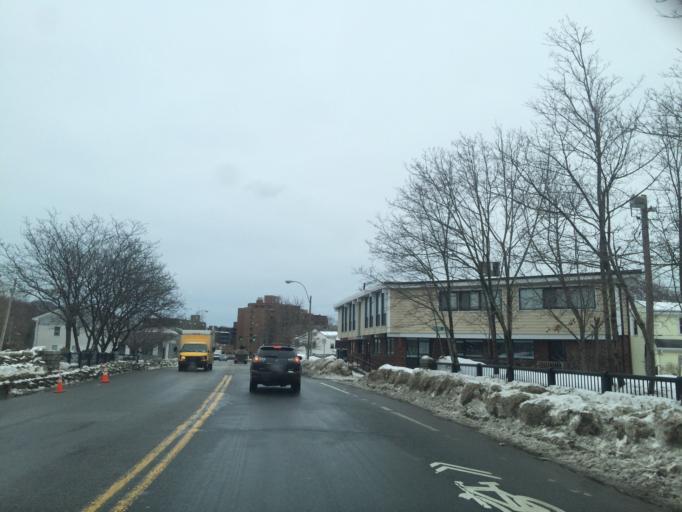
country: US
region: Massachusetts
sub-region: Middlesex County
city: Watertown
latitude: 42.3701
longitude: -71.1933
